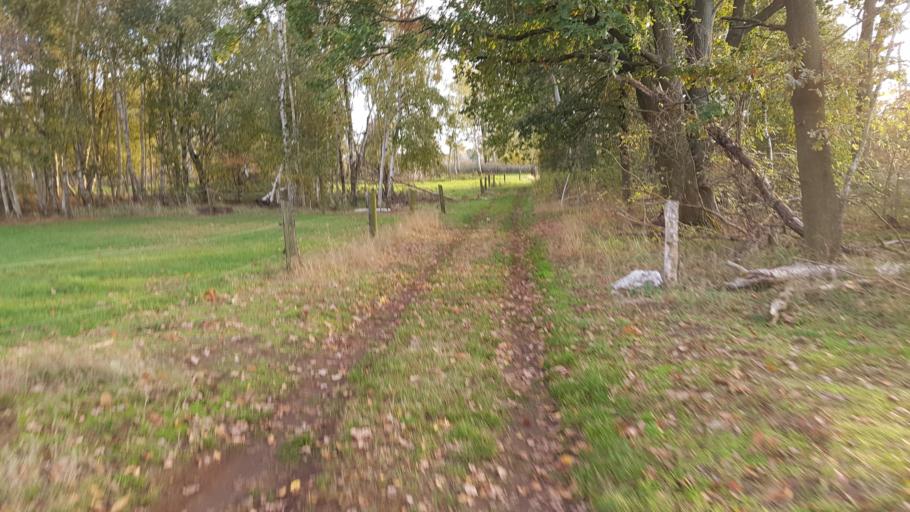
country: DE
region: Brandenburg
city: Schilda
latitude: 51.5681
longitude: 13.4060
